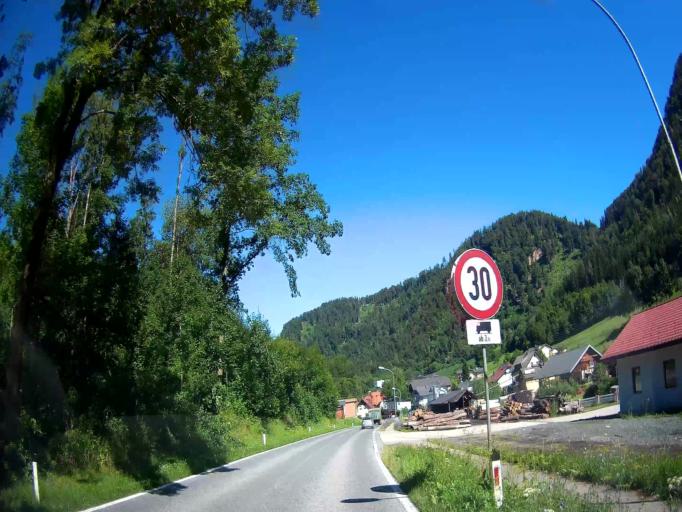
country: AT
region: Carinthia
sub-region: Politischer Bezirk Sankt Veit an der Glan
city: Bruckl
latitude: 46.7230
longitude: 14.5504
